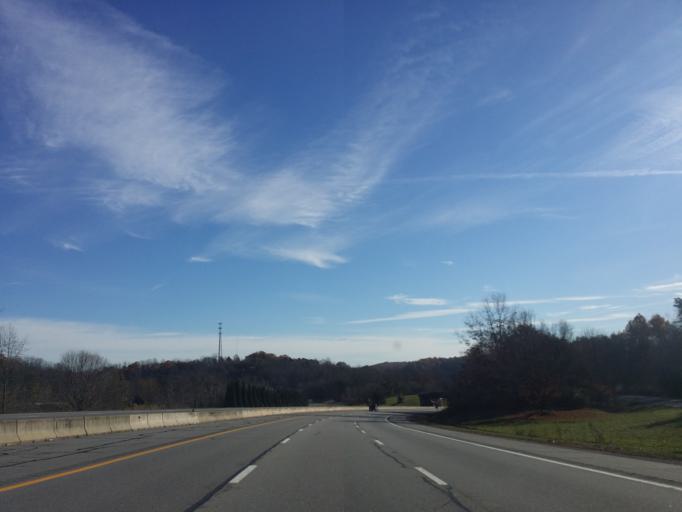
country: US
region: North Carolina
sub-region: Buncombe County
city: Black Mountain
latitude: 35.6235
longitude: -82.1980
